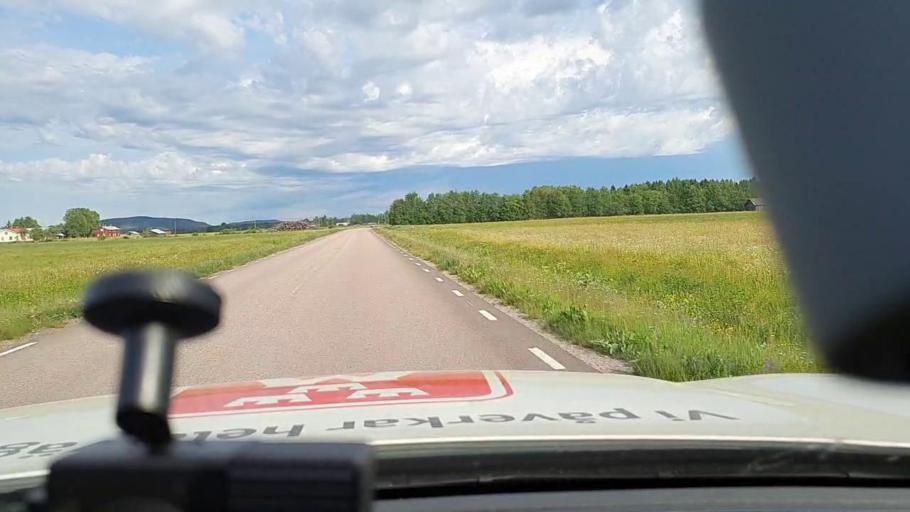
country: SE
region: Norrbotten
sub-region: Bodens Kommun
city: Saevast
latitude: 65.6979
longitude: 21.7753
